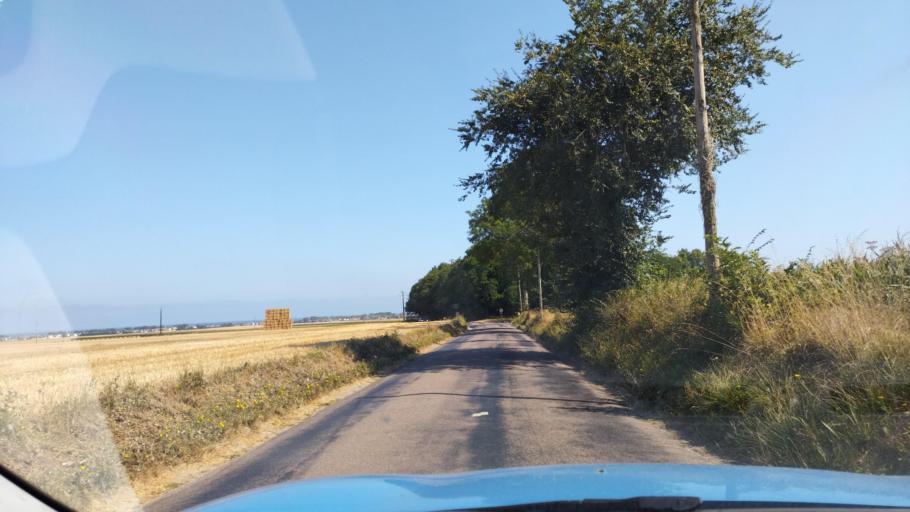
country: FR
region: Lower Normandy
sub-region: Departement du Calvados
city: Bernieres-sur-Mer
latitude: 49.3081
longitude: -0.4067
